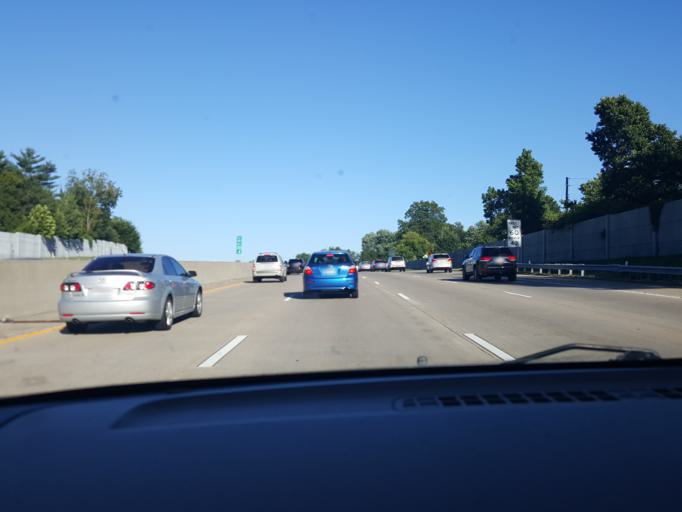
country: US
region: Missouri
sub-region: Saint Louis County
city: Ladue
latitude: 38.6305
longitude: -90.3683
